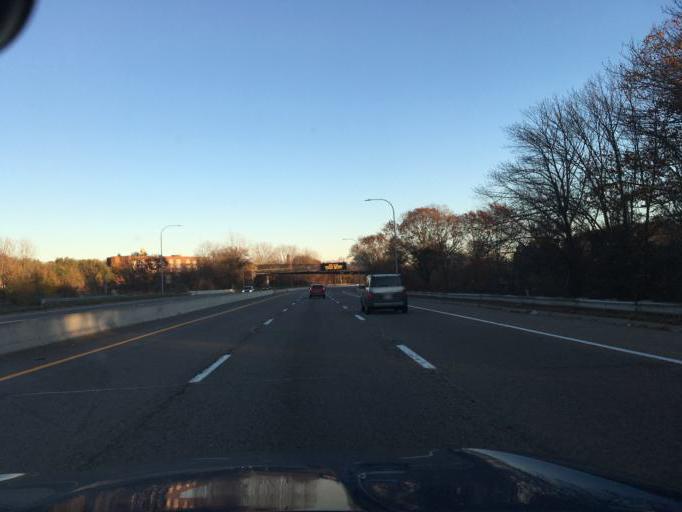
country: US
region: Rhode Island
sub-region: Providence County
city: North Providence
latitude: 41.8219
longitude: -71.4554
